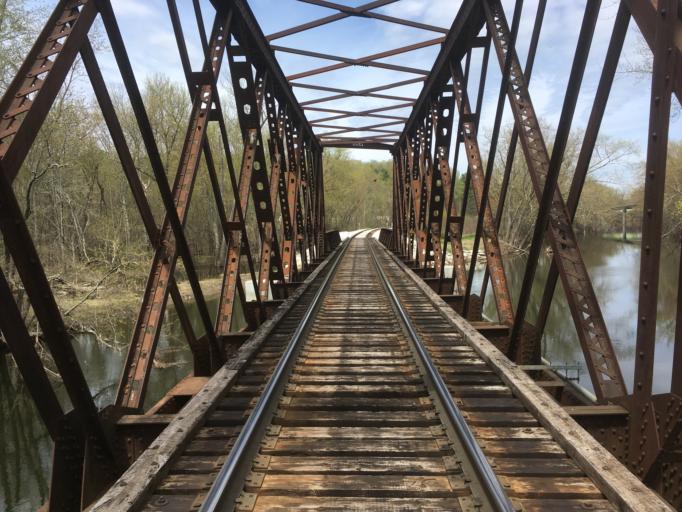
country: US
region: Vermont
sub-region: Rutland County
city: Brandon
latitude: 43.7171
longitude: -73.0514
